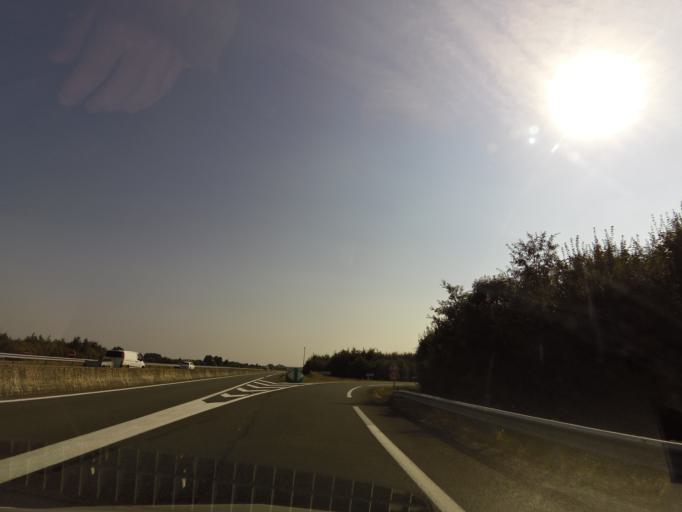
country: FR
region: Pays de la Loire
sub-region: Departement de la Vendee
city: Les Essarts
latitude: 46.8084
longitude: -1.2073
